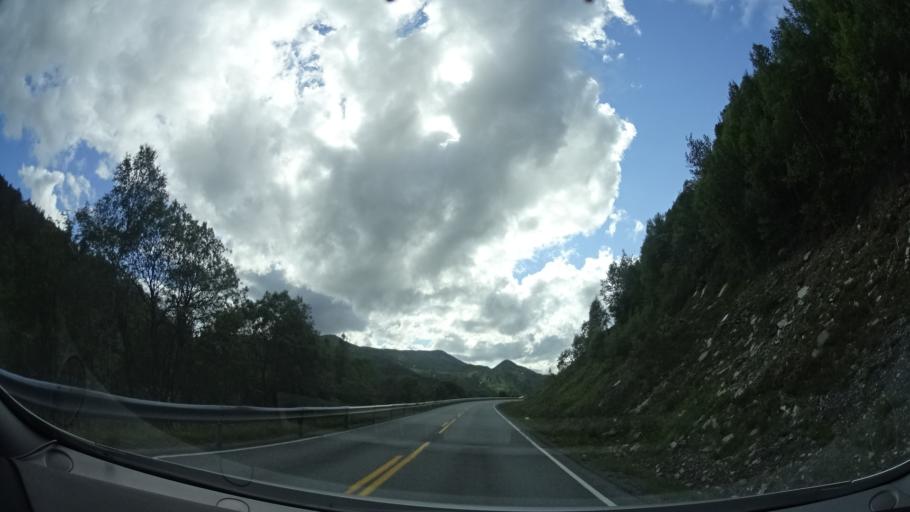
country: NO
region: More og Romsdal
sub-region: Rindal
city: Rindal
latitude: 63.2220
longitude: 9.2854
